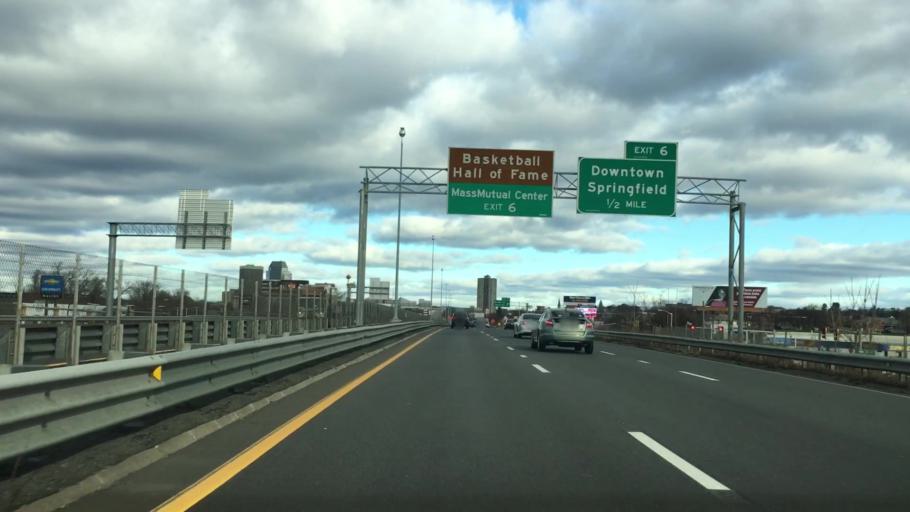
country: US
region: Massachusetts
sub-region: Hampden County
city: Springfield
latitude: 42.0868
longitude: -72.5804
